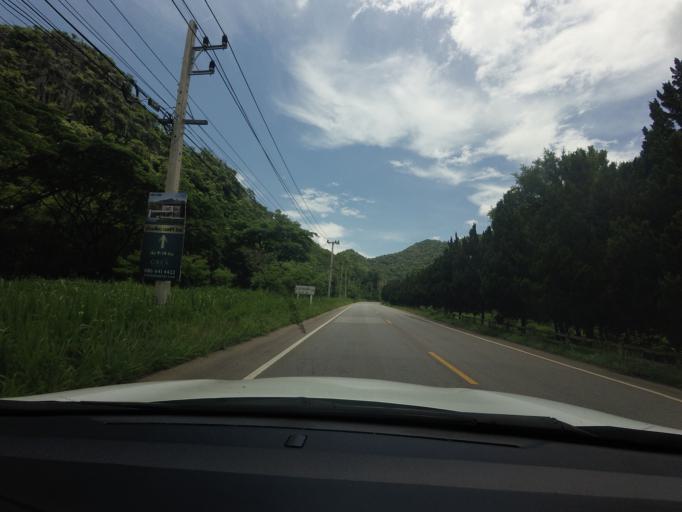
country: TH
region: Sara Buri
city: Muak Lek
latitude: 14.5724
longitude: 101.2874
